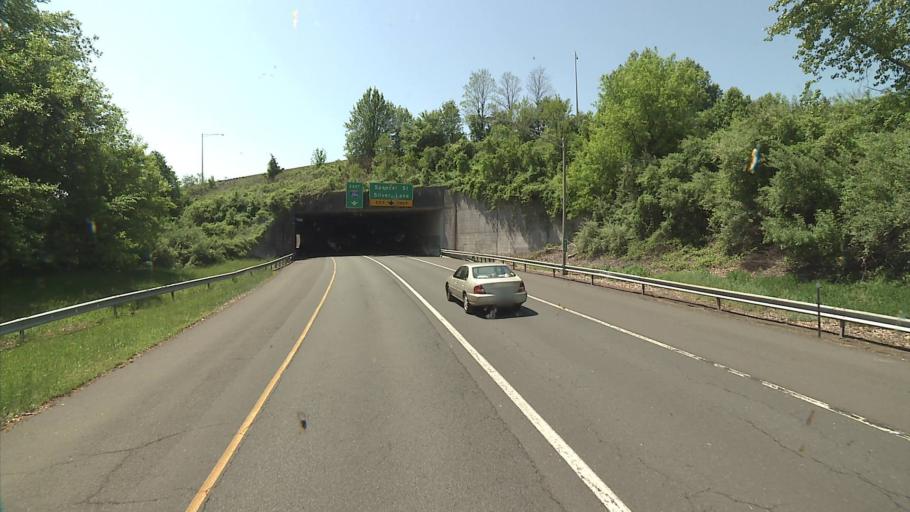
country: US
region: Connecticut
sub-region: Hartford County
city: East Hartford
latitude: 41.7728
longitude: -72.5803
